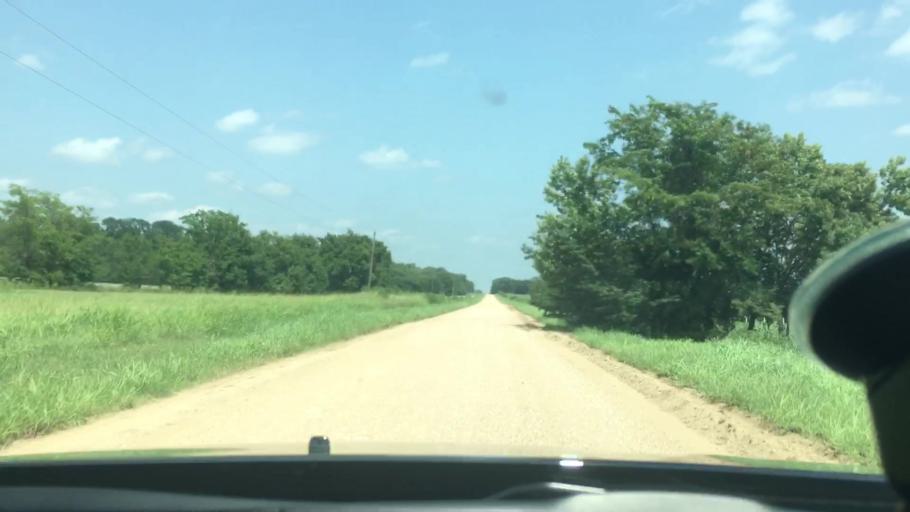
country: US
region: Oklahoma
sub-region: Johnston County
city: Tishomingo
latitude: 34.4224
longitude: -96.4739
